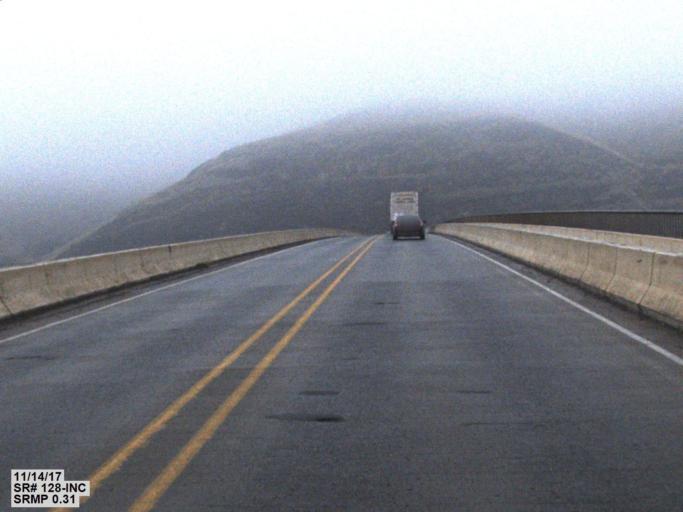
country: US
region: Washington
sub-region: Asotin County
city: West Clarkston-Highland
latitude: 46.4240
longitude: -117.0715
